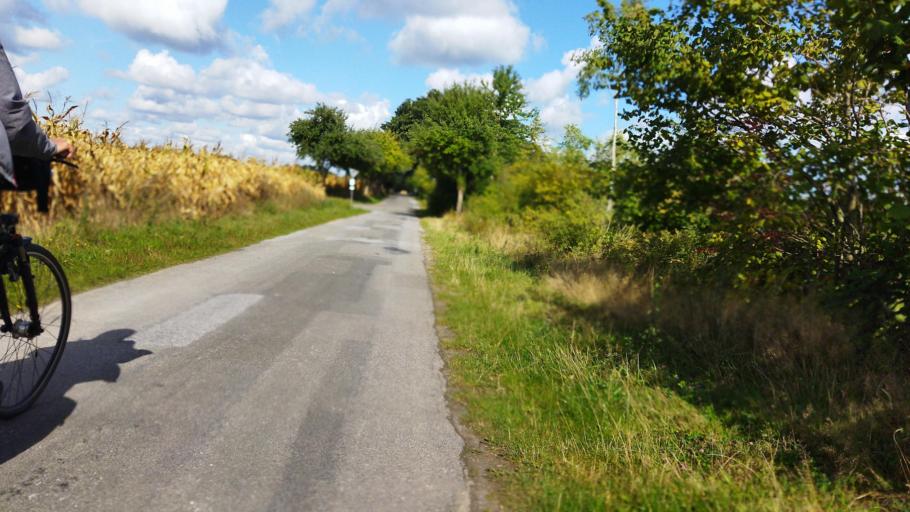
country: DE
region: Lower Saxony
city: Salzbergen
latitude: 52.3700
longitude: 7.3345
